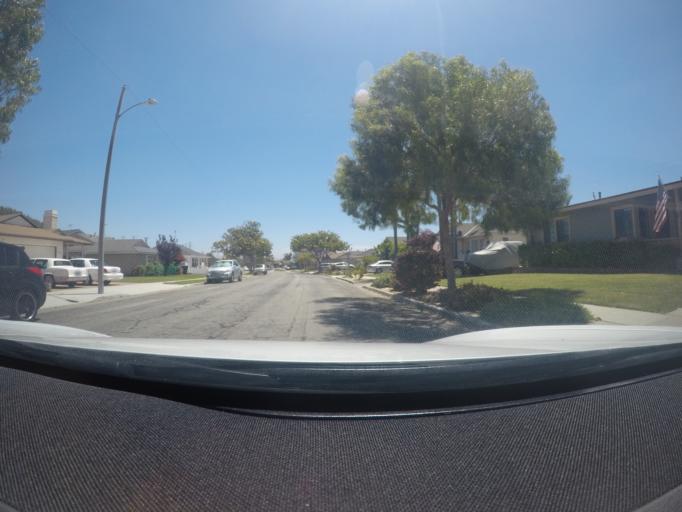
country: US
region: California
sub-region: Los Angeles County
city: Torrance
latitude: 33.8550
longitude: -118.3589
